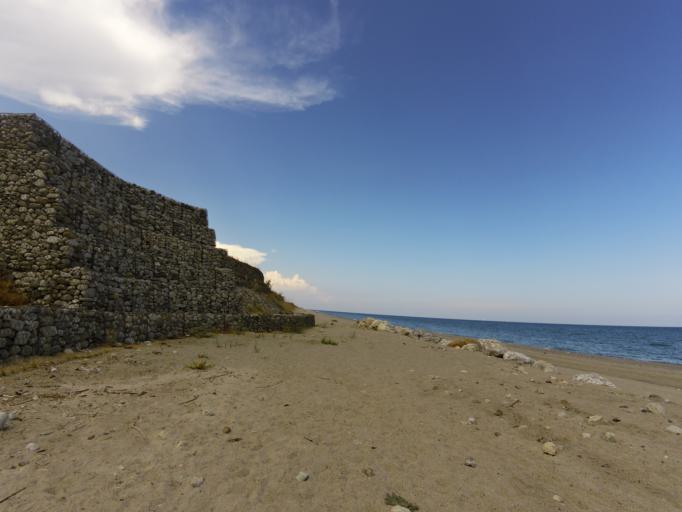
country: IT
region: Calabria
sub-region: Provincia di Reggio Calabria
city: Monasterace Marina
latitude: 38.4453
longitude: 16.5791
